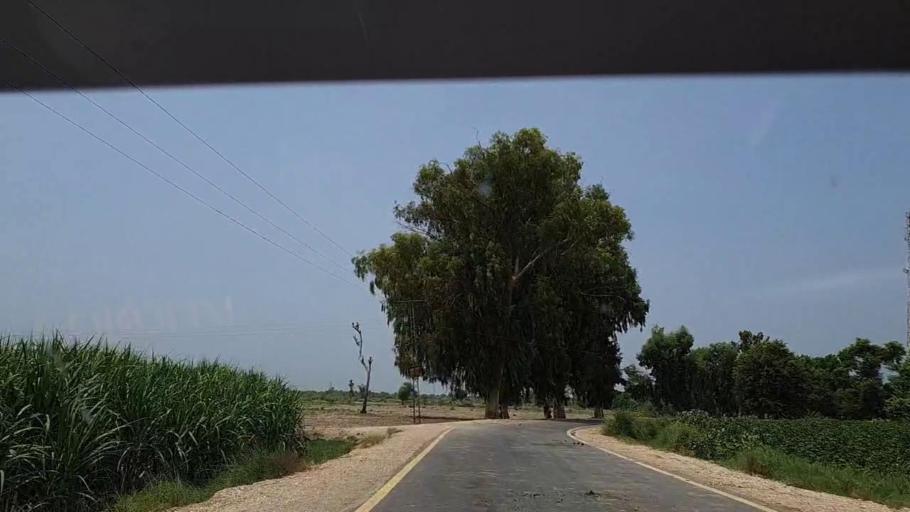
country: PK
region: Sindh
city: Adilpur
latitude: 27.8740
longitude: 69.2777
